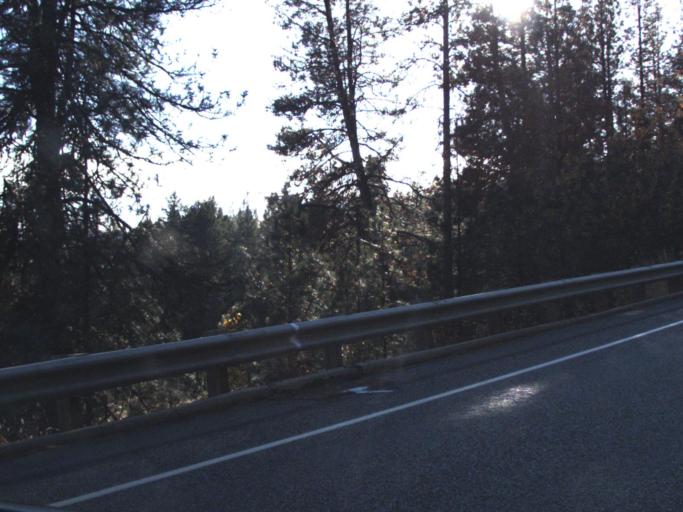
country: CA
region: British Columbia
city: Rossland
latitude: 48.9456
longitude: -117.7800
